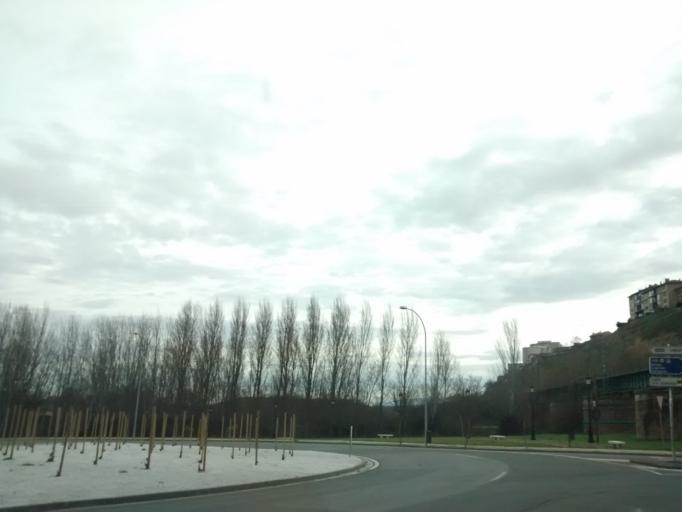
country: ES
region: La Rioja
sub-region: Provincia de La Rioja
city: Haro
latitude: 42.5821
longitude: -2.8467
